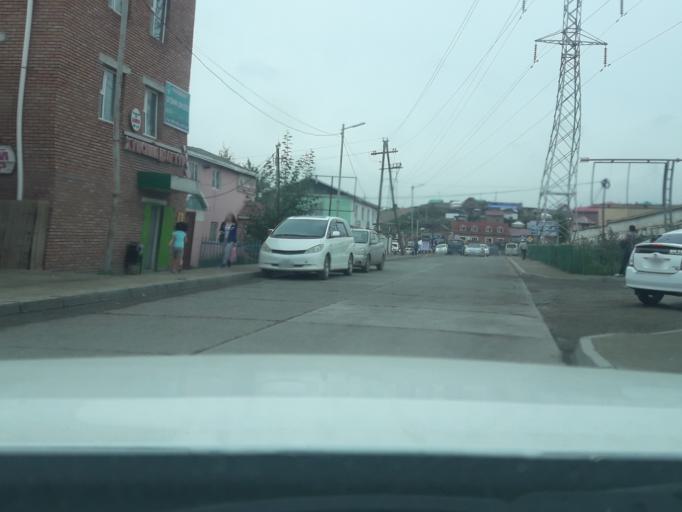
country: MN
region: Ulaanbaatar
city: Ulaanbaatar
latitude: 47.9468
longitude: 106.9034
